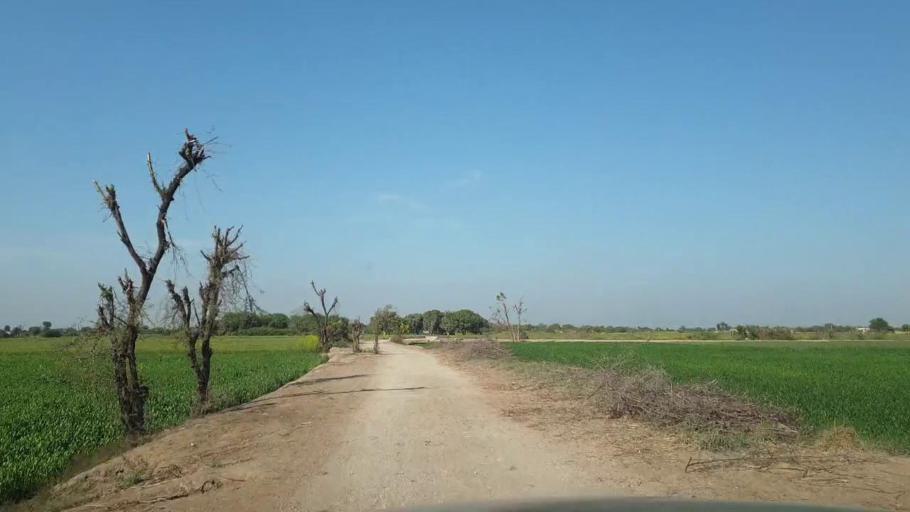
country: PK
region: Sindh
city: Tando Adam
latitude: 25.6793
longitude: 68.6880
